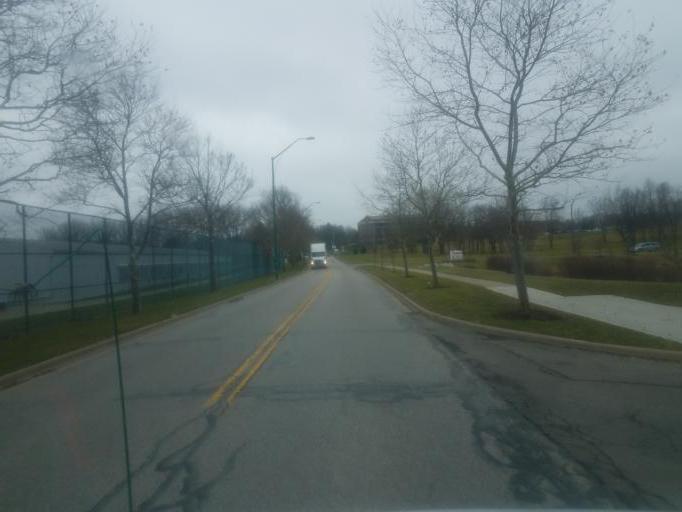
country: US
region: Ohio
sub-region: Franklin County
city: Westerville
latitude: 40.1134
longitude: -82.9427
